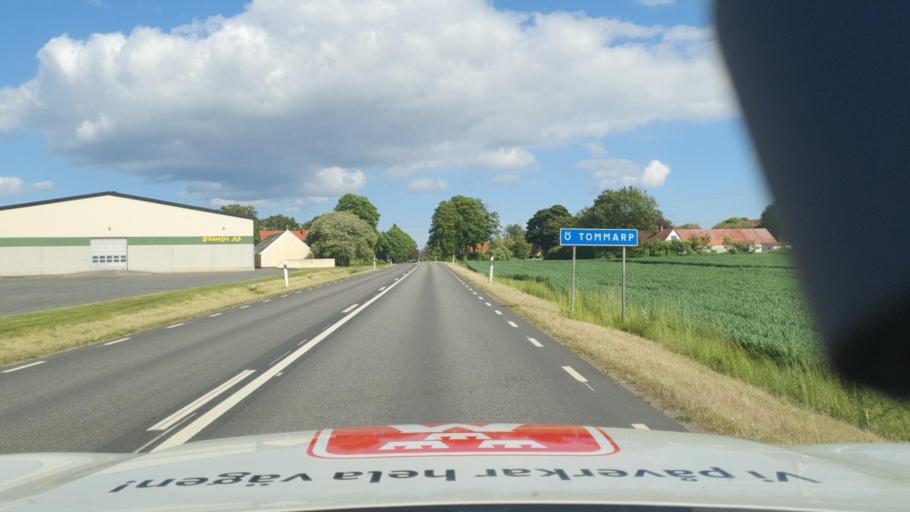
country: SE
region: Skane
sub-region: Simrishamns Kommun
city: Simrishamn
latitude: 55.5350
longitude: 14.2349
